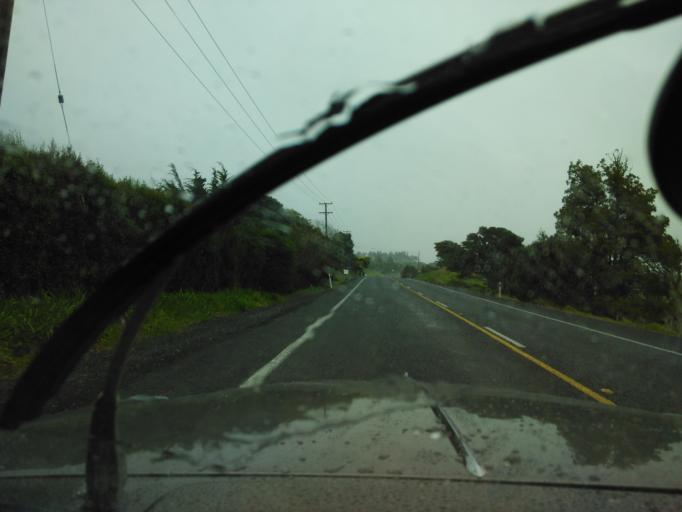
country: NZ
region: Auckland
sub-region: Auckland
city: Wellsford
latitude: -36.3043
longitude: 174.4997
